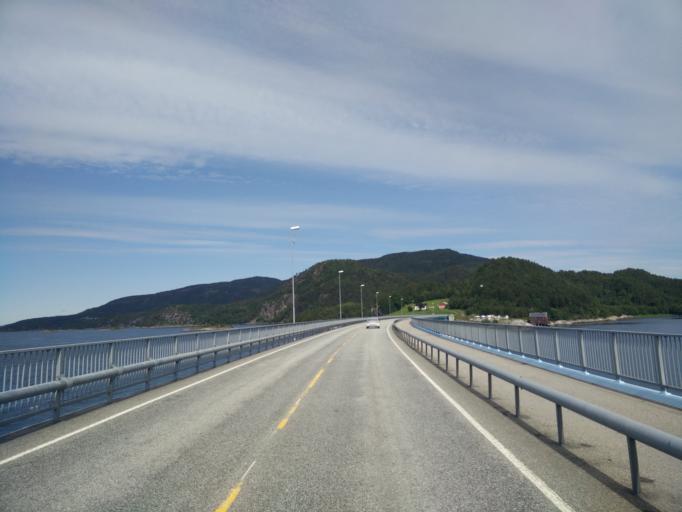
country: NO
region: More og Romsdal
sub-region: Kristiansund
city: Rensvik
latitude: 62.9870
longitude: 7.8745
